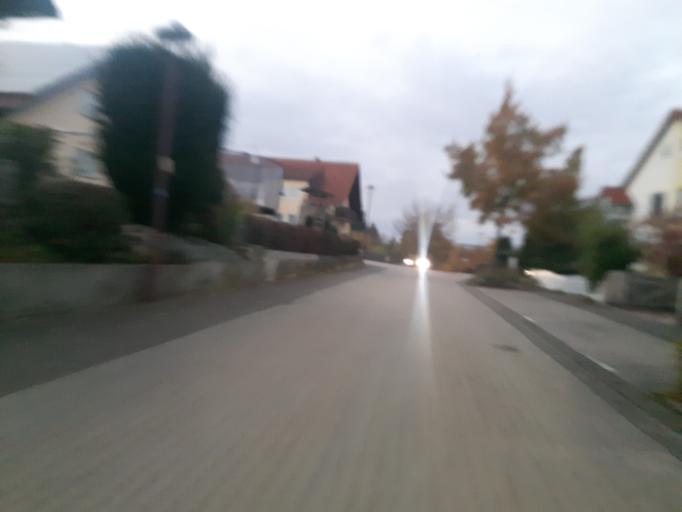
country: DE
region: Rheinland-Pfalz
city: Ober-Florsheim
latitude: 49.6871
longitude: 8.1568
